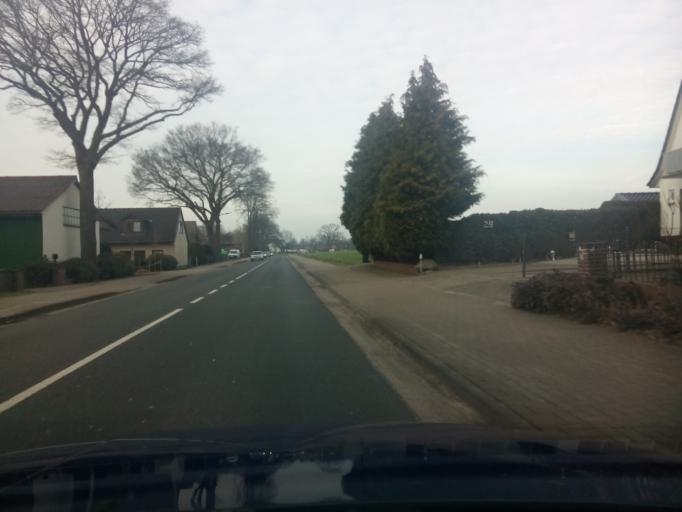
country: DE
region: Lower Saxony
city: Oyten
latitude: 53.0634
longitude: 9.0213
